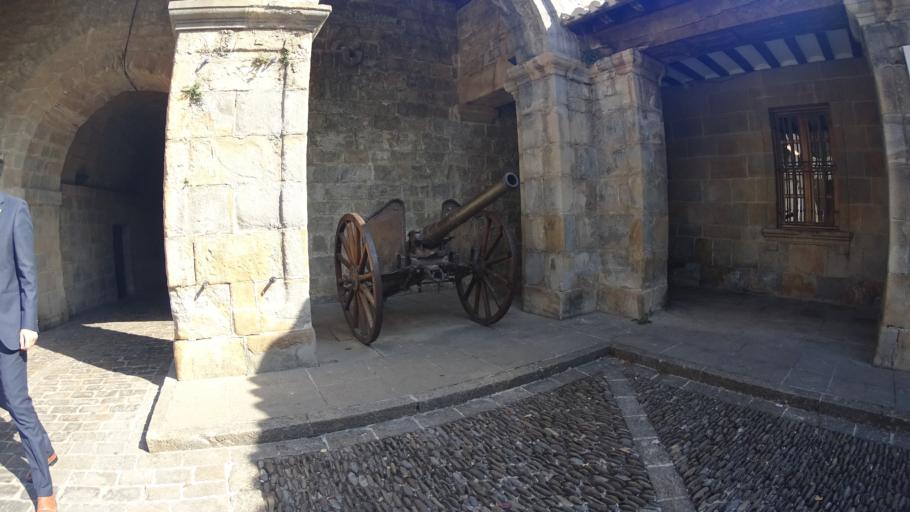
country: ES
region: Navarre
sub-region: Provincia de Navarra
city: Primer Ensanche
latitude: 42.8130
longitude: -1.6487
